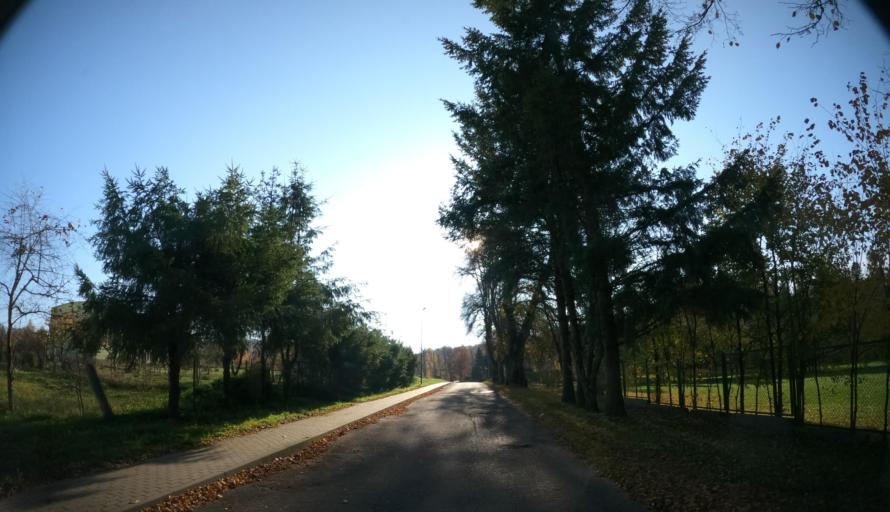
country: PL
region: Pomeranian Voivodeship
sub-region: Powiat slupski
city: Kepice
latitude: 54.2199
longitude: 16.8556
